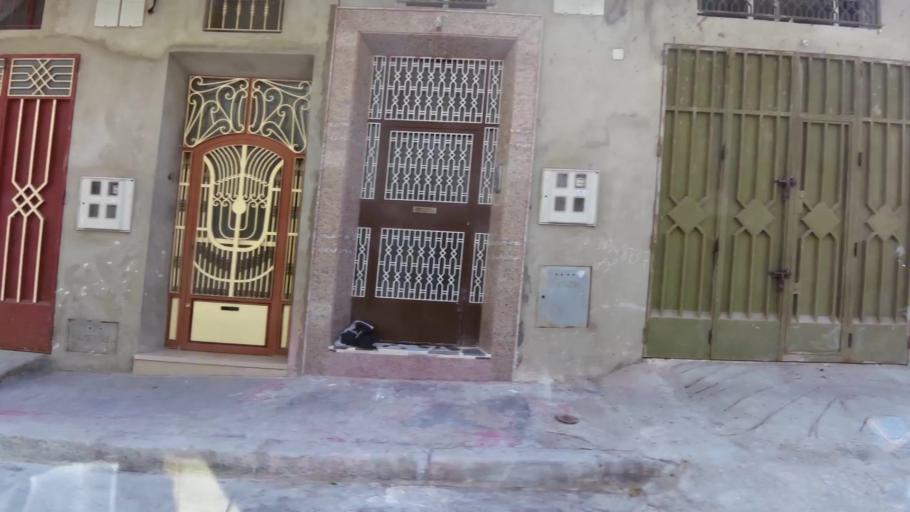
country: MA
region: Tanger-Tetouan
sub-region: Tanger-Assilah
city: Tangier
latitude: 35.7504
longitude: -5.8115
